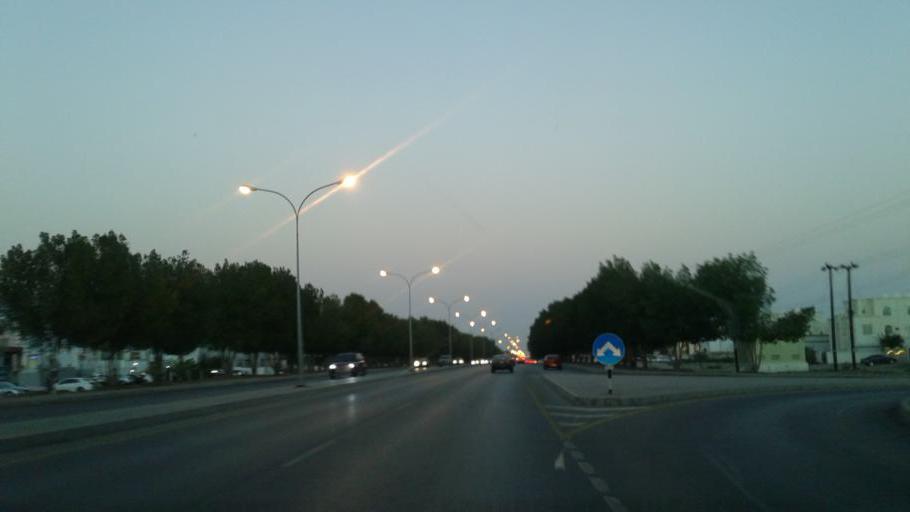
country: OM
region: Muhafazat Masqat
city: As Sib al Jadidah
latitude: 23.6141
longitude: 58.2212
